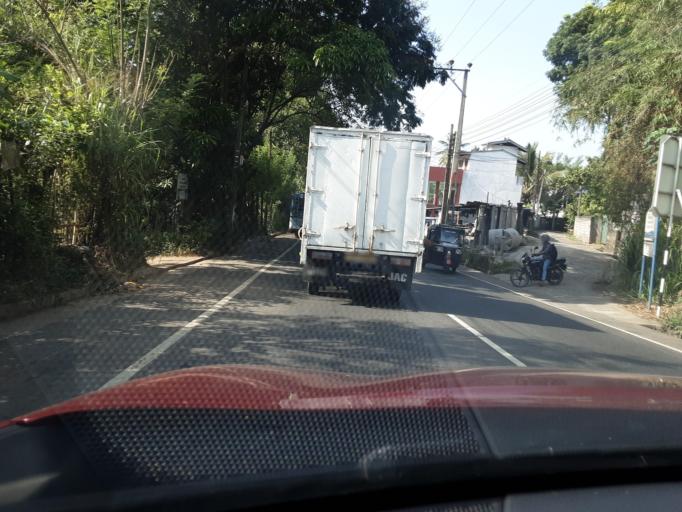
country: LK
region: Uva
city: Badulla
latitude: 6.9843
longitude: 81.0643
